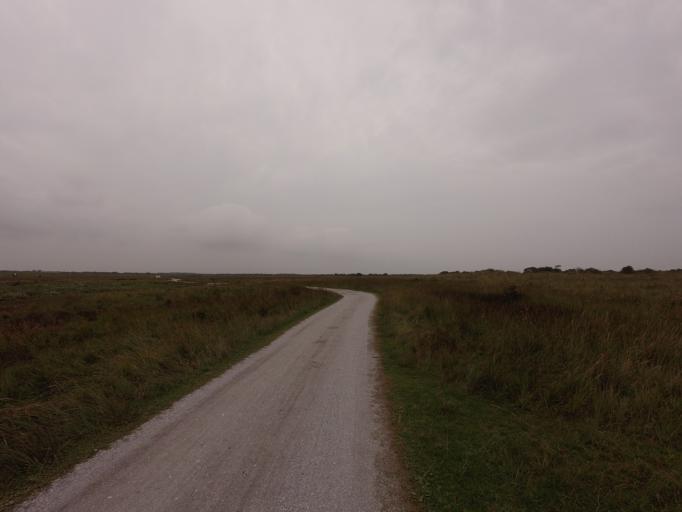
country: NL
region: Friesland
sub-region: Gemeente Schiermonnikoog
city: Schiermonnikoog
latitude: 53.4870
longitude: 6.2126
